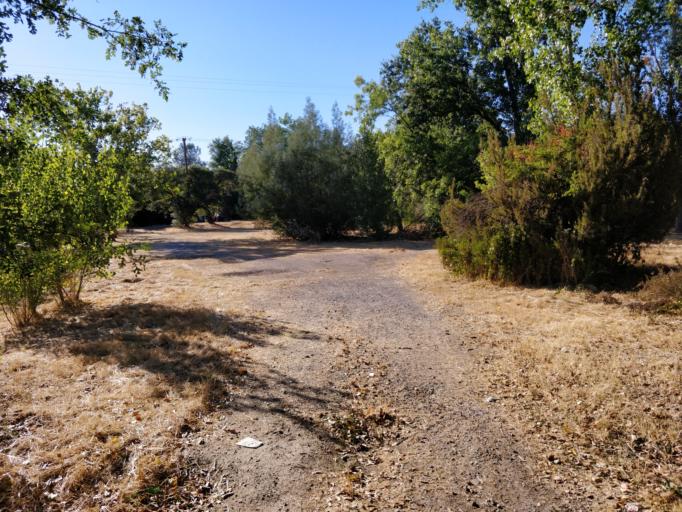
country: US
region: California
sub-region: Shasta County
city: Shasta Lake
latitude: 40.6769
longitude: -122.3534
